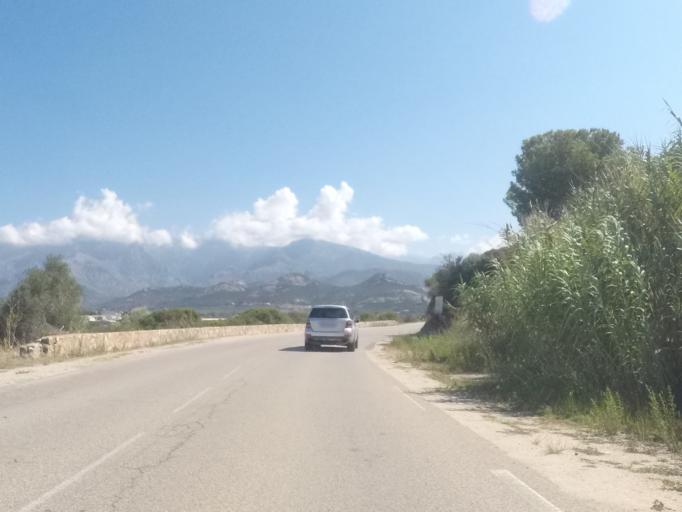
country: FR
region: Corsica
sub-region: Departement de la Haute-Corse
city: Calvi
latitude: 42.5431
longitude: 8.7897
